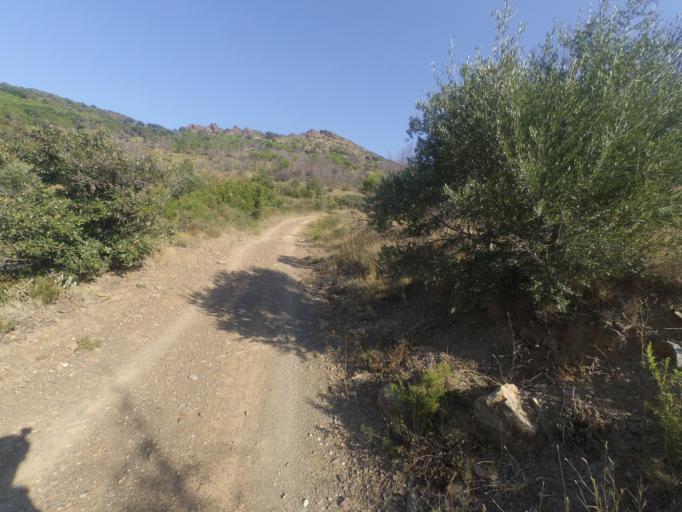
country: FR
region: Languedoc-Roussillon
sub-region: Departement des Pyrenees-Orientales
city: Corneilla-la-Riviere
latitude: 42.7285
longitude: 2.7120
